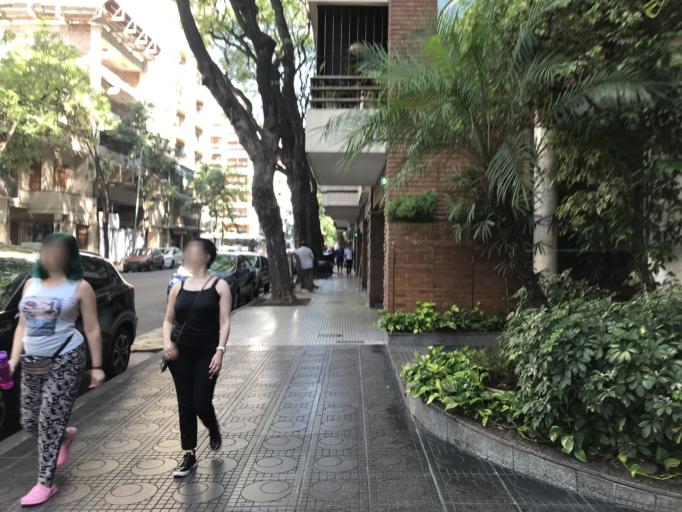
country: AR
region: Buenos Aires F.D.
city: Villa Santa Rita
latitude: -34.6275
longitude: -58.4508
